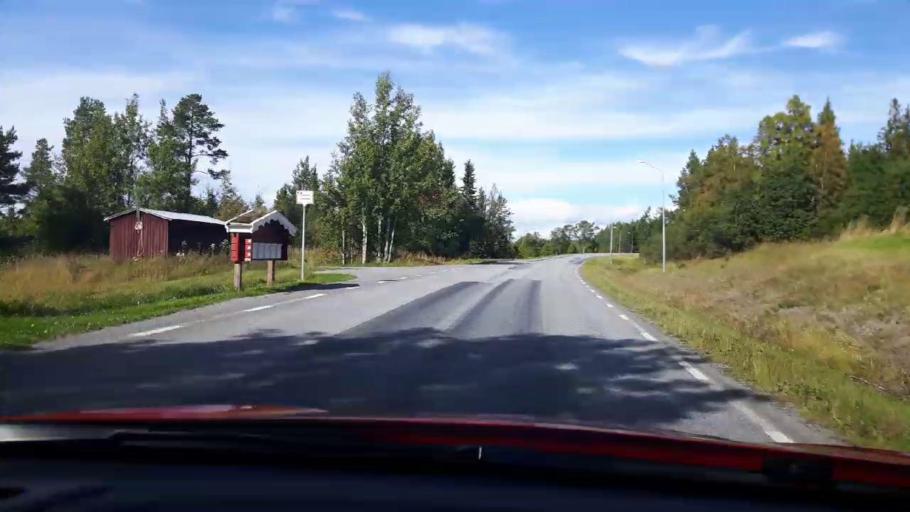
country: SE
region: Jaemtland
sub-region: OEstersunds Kommun
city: Ostersund
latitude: 63.0881
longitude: 14.4362
